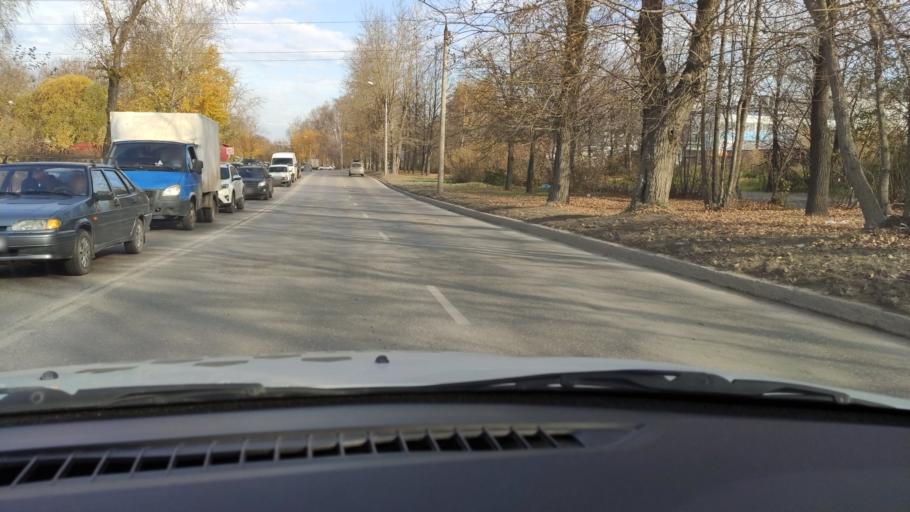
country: RU
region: Perm
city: Froly
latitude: 57.9553
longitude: 56.2416
